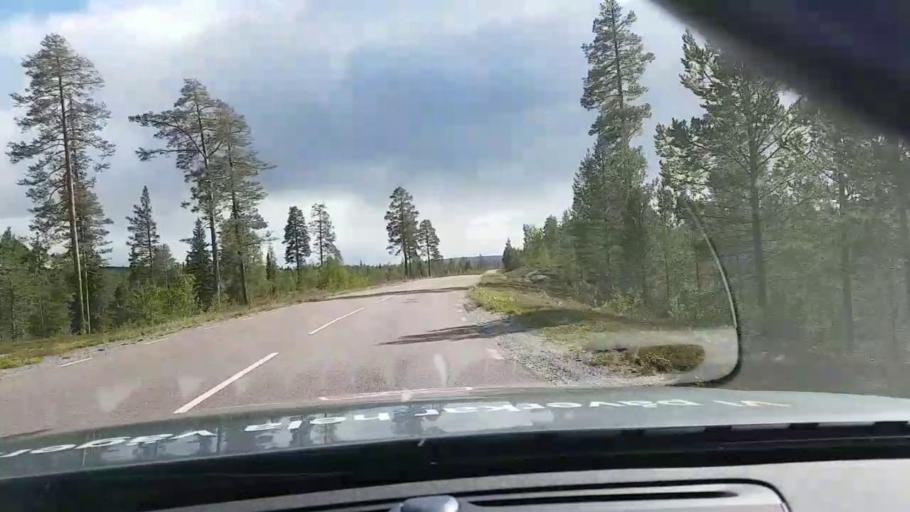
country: SE
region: Vaesterbotten
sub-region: Asele Kommun
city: Asele
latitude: 63.9019
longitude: 17.3475
